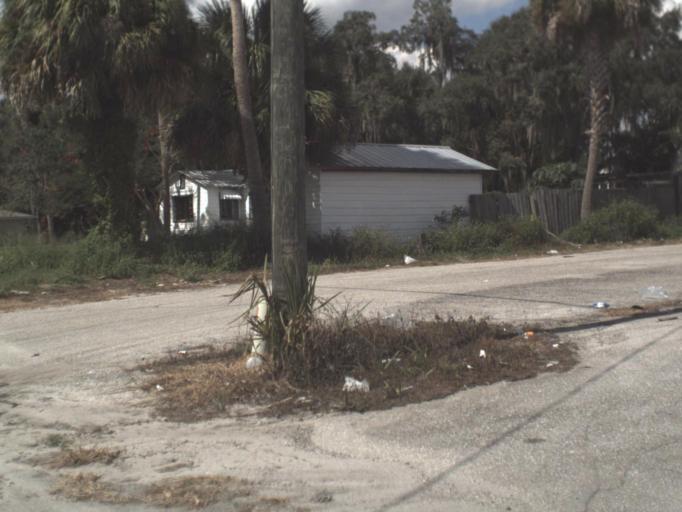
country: US
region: Florida
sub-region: Hardee County
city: Zolfo Springs
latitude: 27.4935
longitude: -81.7967
